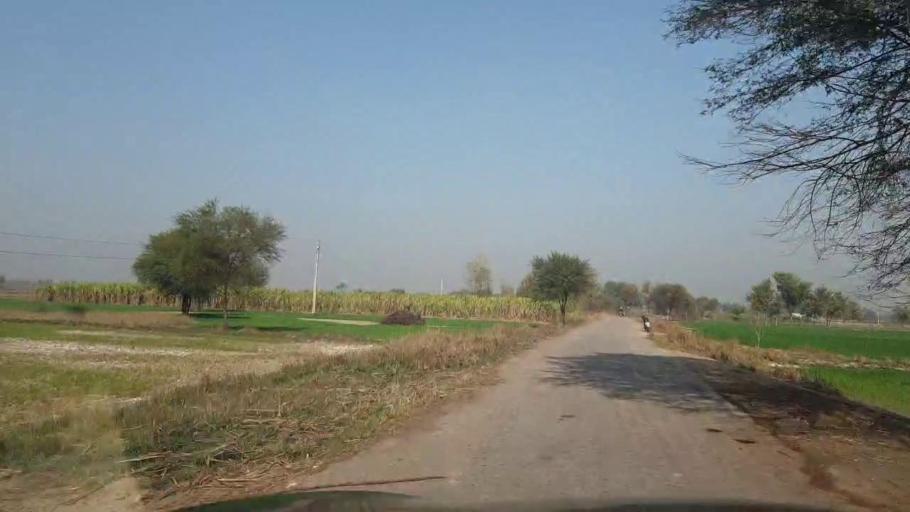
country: PK
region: Sindh
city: Ubauro
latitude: 28.1331
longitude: 69.7694
